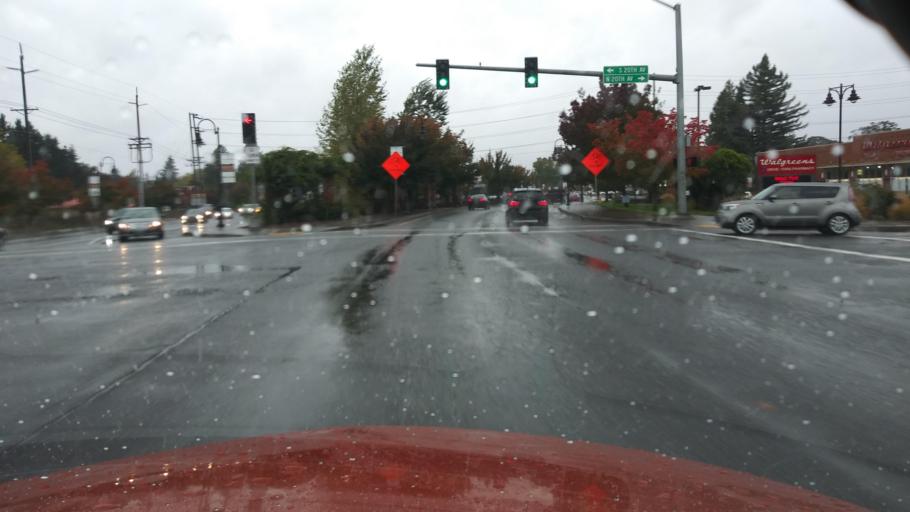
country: US
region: Oregon
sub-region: Washington County
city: Cornelius
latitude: 45.5203
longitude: -123.0467
